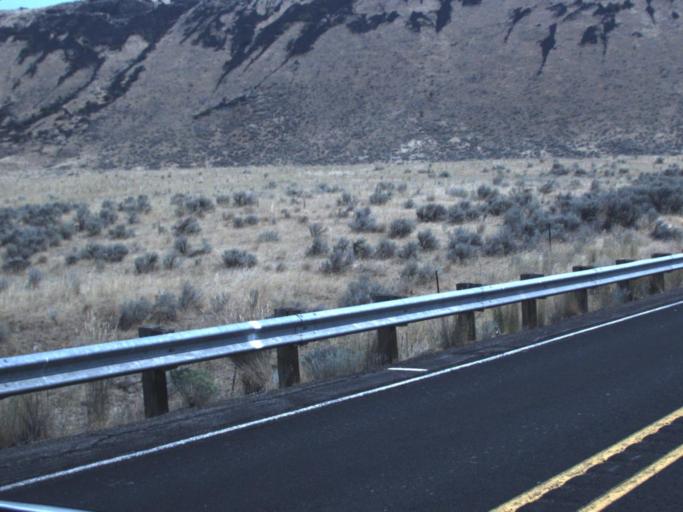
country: US
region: Washington
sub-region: Kittitas County
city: Kittitas
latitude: 46.8526
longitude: -120.4631
